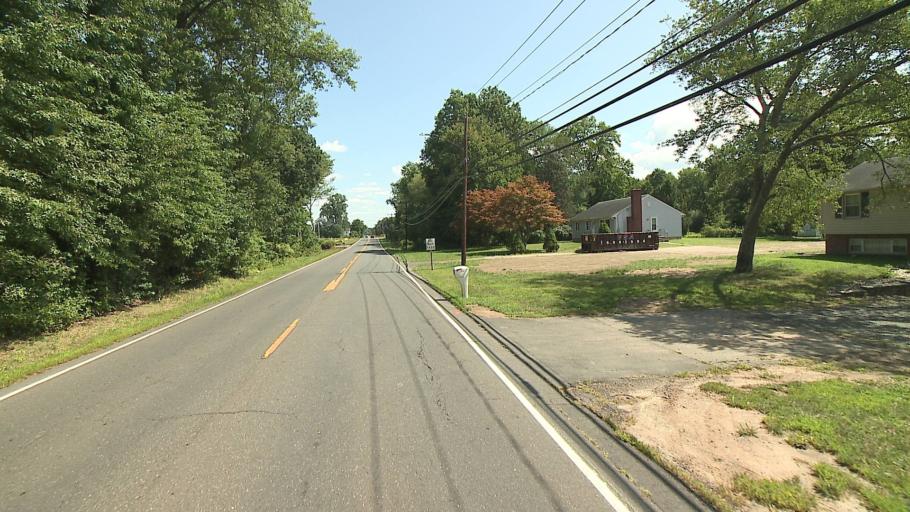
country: US
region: Connecticut
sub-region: Hartford County
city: Southwood Acres
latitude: 41.9336
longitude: -72.5864
